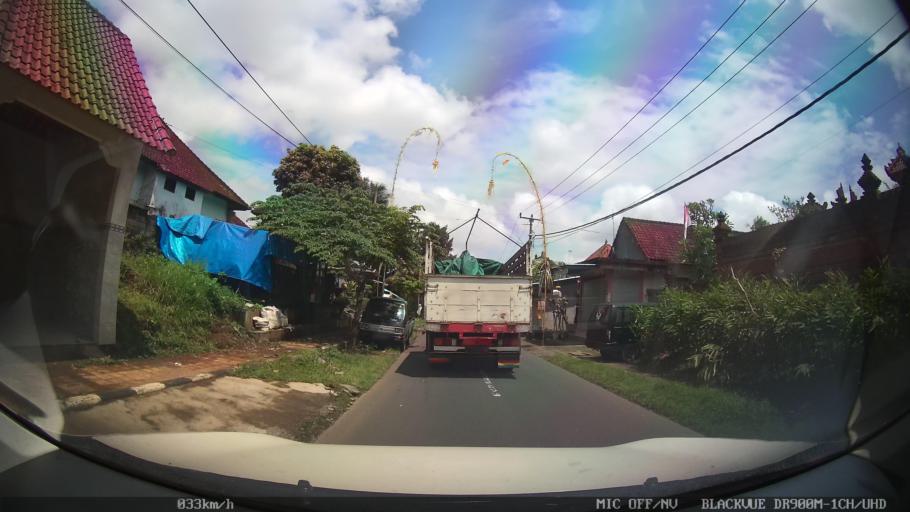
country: ID
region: Bali
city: Banjar Kelodan
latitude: -8.5013
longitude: 115.3672
